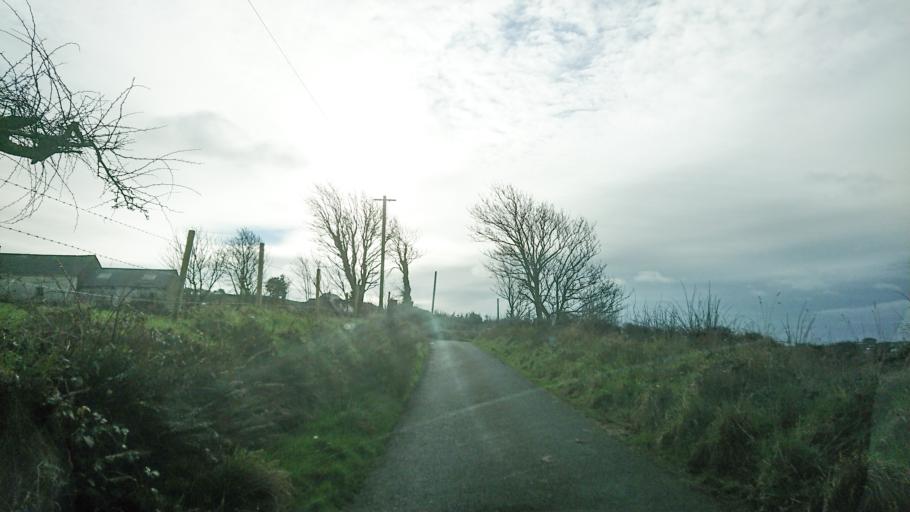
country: IE
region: Munster
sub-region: Waterford
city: Tra Mhor
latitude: 52.1502
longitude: -7.1925
